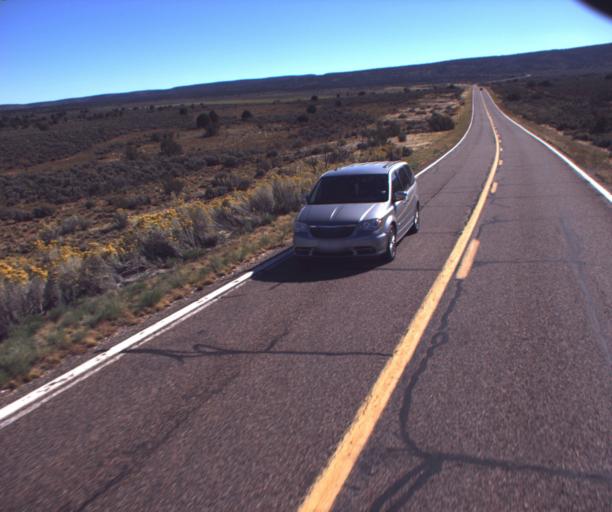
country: US
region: Arizona
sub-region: Coconino County
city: Fredonia
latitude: 36.8581
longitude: -112.3067
